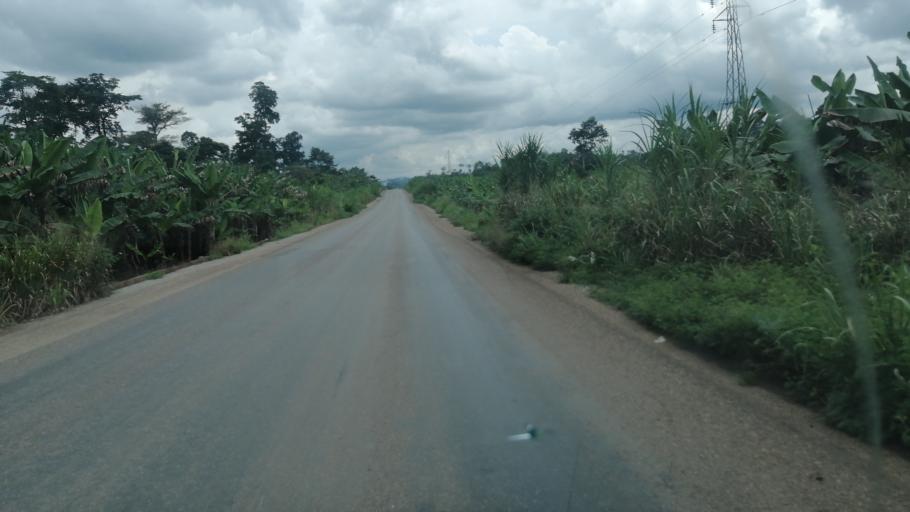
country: GH
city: Duayaw Nkwanta
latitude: 6.9094
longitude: -2.3940
